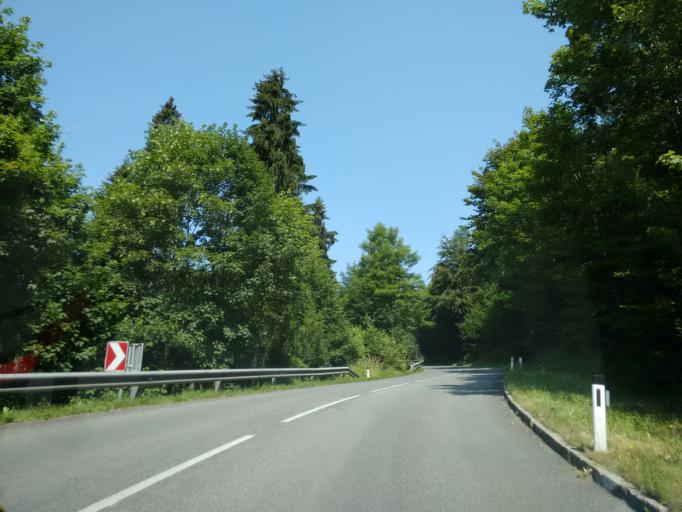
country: AT
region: Upper Austria
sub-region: Politischer Bezirk Urfahr-Umgebung
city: Altenberg bei Linz
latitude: 48.3652
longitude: 14.3317
